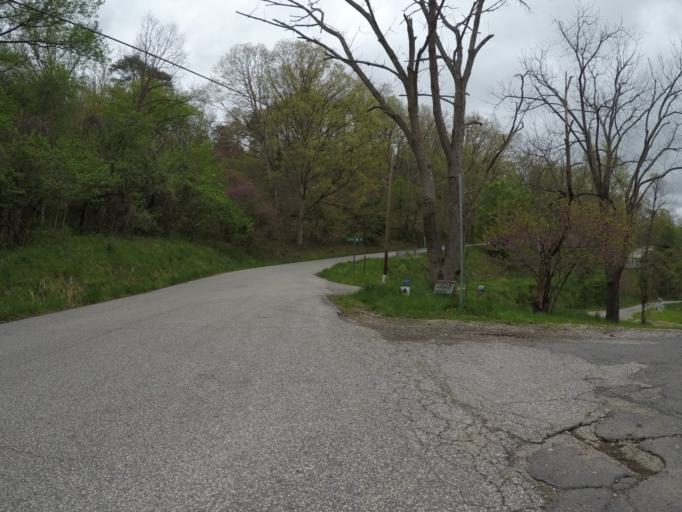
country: US
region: West Virginia
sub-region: Cabell County
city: Barboursville
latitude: 38.4038
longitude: -82.2768
